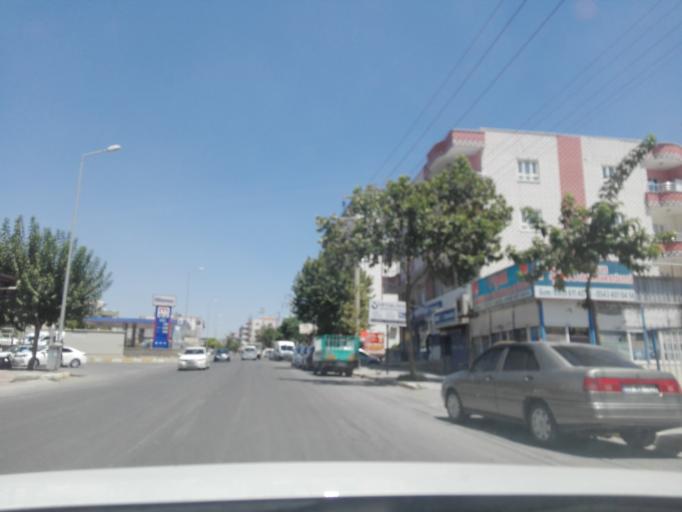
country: TR
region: Batman
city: Batman
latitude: 37.8869
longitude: 41.1441
